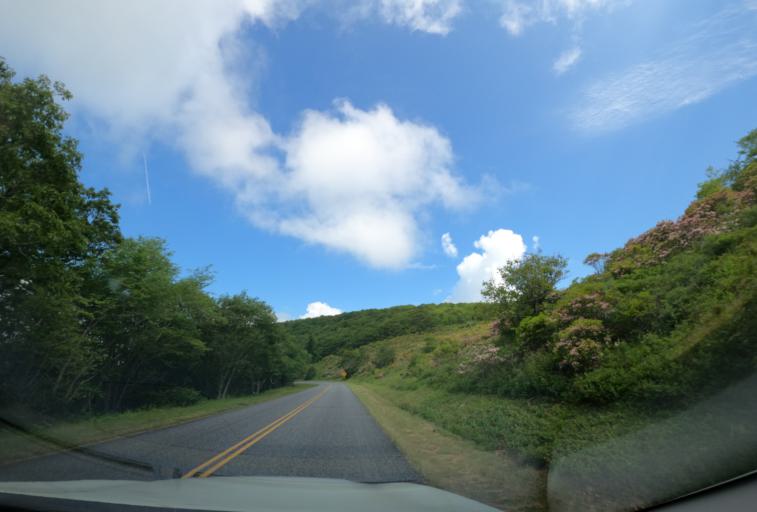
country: US
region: North Carolina
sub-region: Haywood County
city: Hazelwood
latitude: 35.3809
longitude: -83.0265
